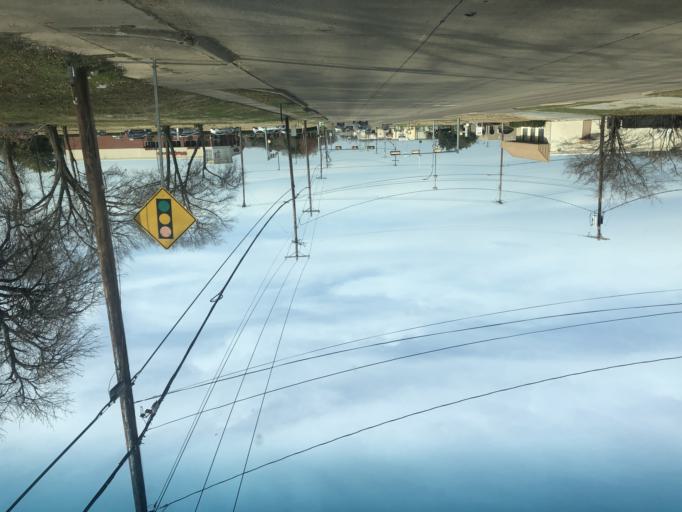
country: US
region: Texas
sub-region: Tarrant County
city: Dalworthington Gardens
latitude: 32.7068
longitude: -97.1504
